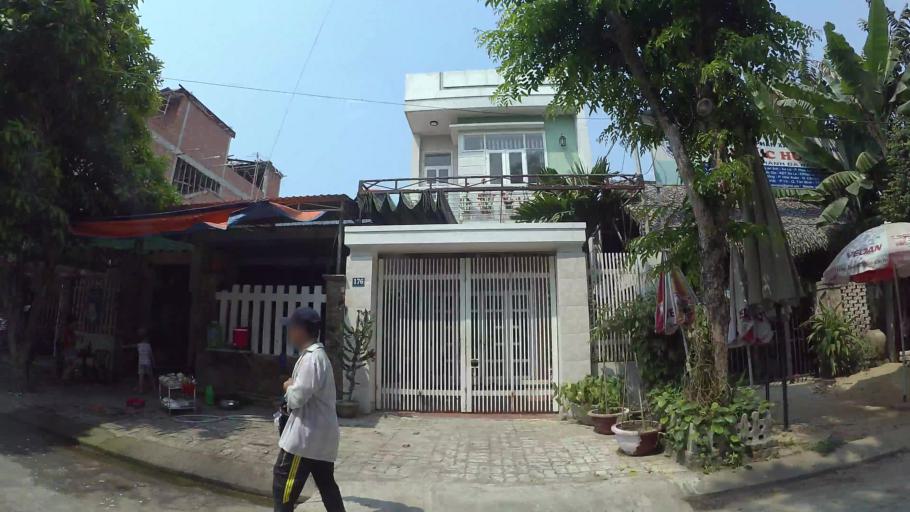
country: VN
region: Da Nang
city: Cam Le
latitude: 15.9861
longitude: 108.2089
